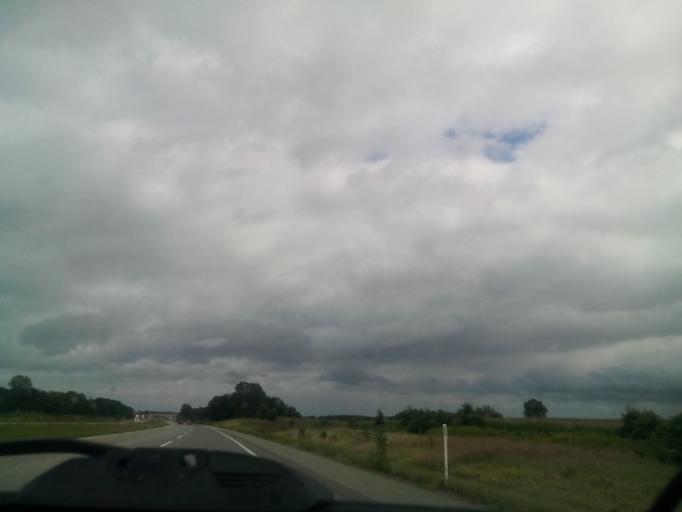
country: US
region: Indiana
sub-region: Steuben County
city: Fremont
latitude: 41.6937
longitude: -84.9064
